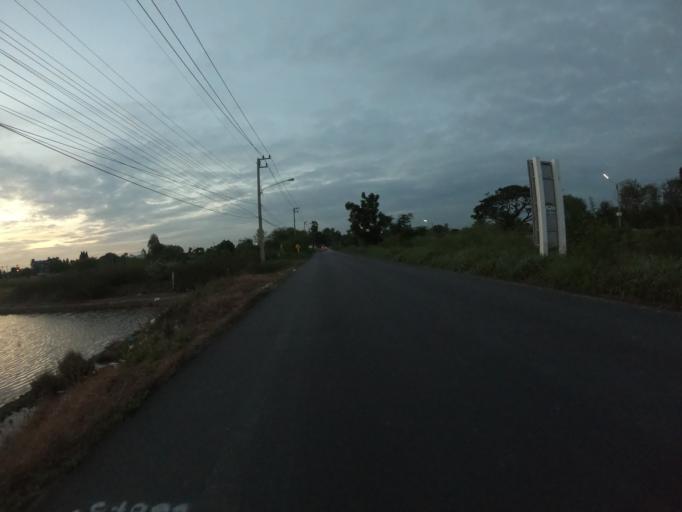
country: TH
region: Pathum Thani
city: Ban Rangsit
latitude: 14.0410
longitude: 100.8009
